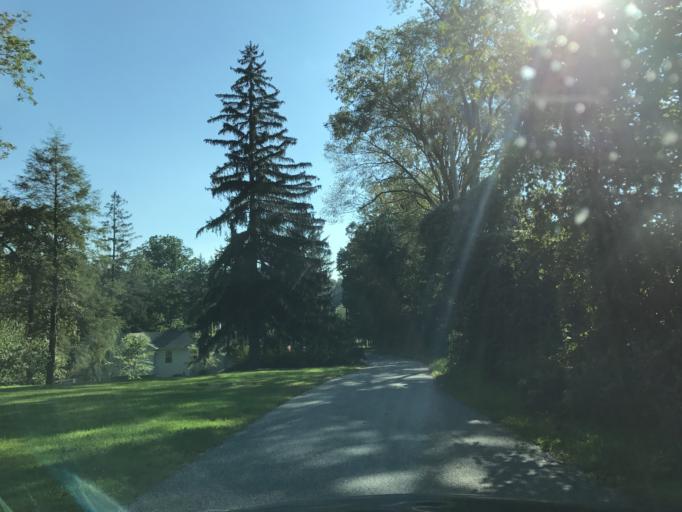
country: US
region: Maryland
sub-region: Baltimore County
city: Hunt Valley
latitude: 39.5364
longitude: -76.5979
